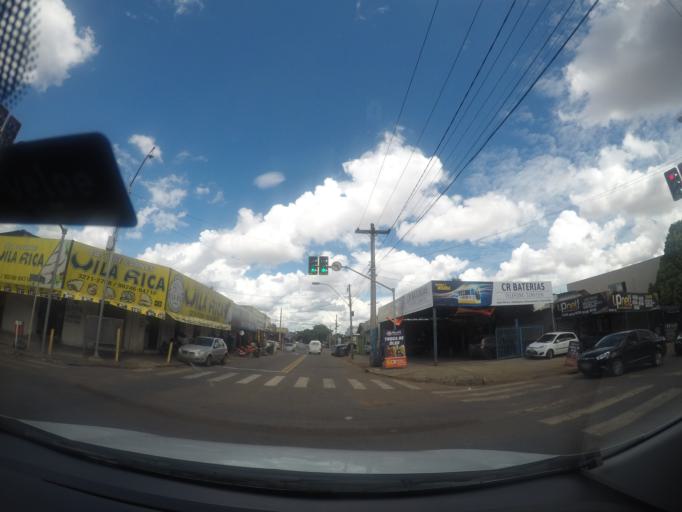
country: BR
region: Goias
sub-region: Goiania
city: Goiania
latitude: -16.6629
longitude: -49.3030
